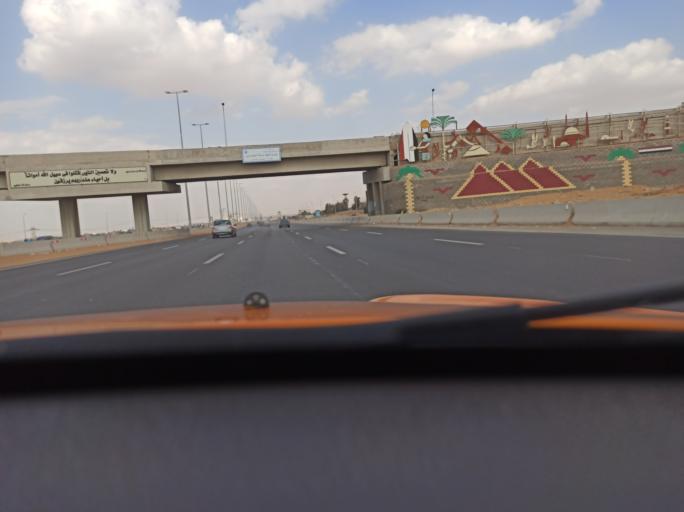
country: EG
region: Eastern Province
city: Bilbays
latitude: 30.1841
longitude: 31.6184
